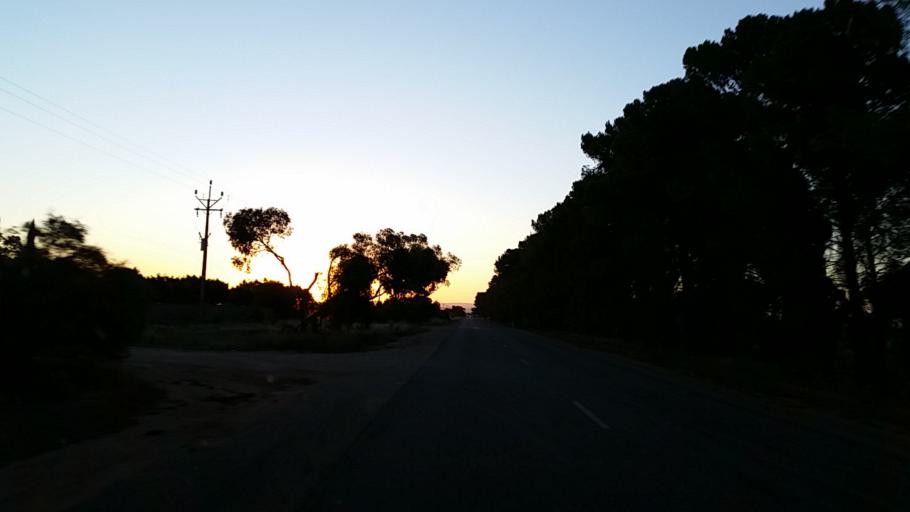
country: AU
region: South Australia
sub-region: Clare and Gilbert Valleys
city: Clare
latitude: -33.8493
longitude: 138.4810
